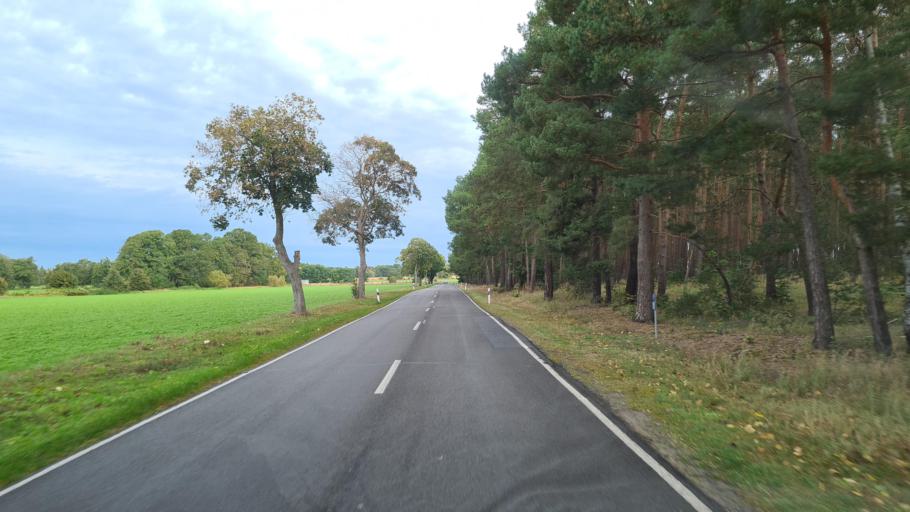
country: DE
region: Brandenburg
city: Kasel-Golzig
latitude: 51.9215
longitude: 13.7109
